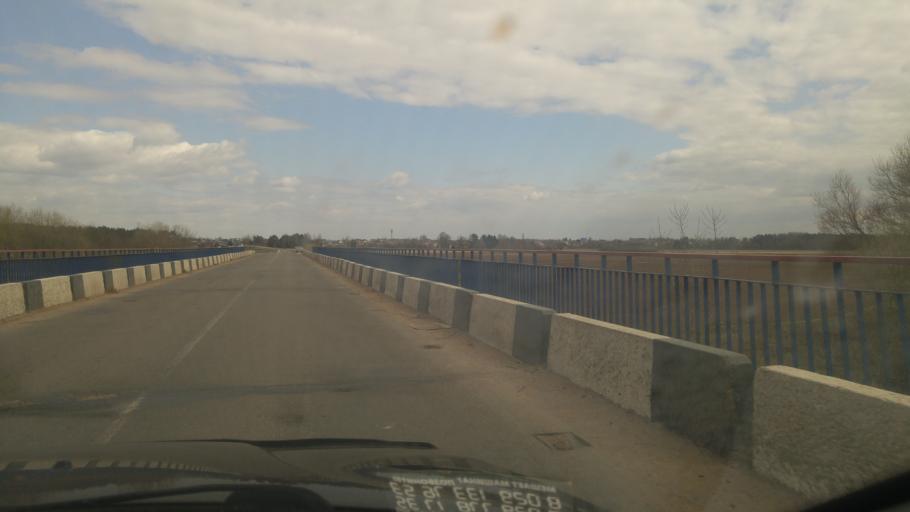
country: BY
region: Minsk
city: Rudzyensk
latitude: 53.6558
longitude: 27.8120
